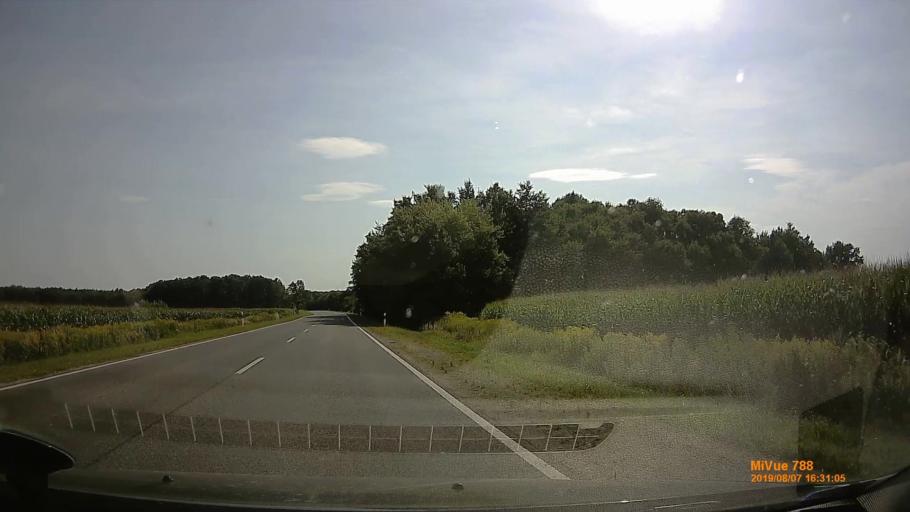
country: HU
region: Zala
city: Lenti
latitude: 46.6613
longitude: 16.5037
